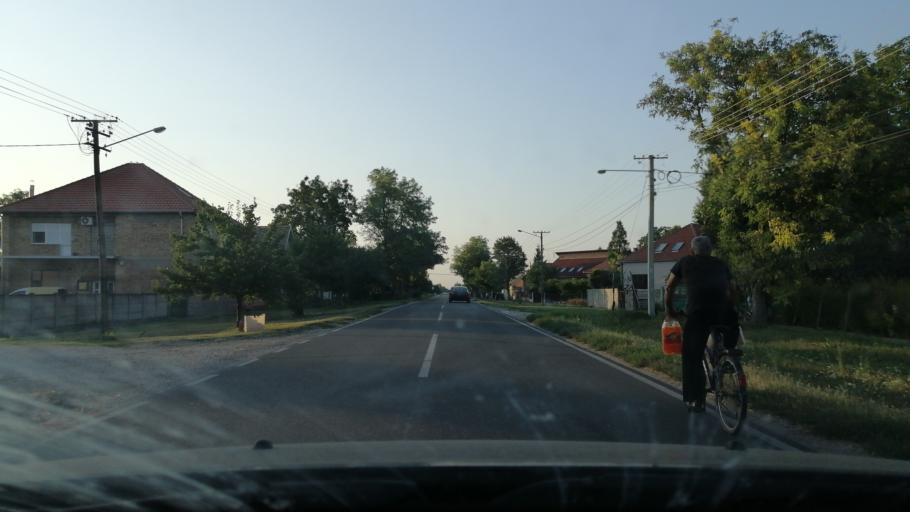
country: RS
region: Central Serbia
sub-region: Belgrade
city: Grocka
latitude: 44.7639
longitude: 20.7331
